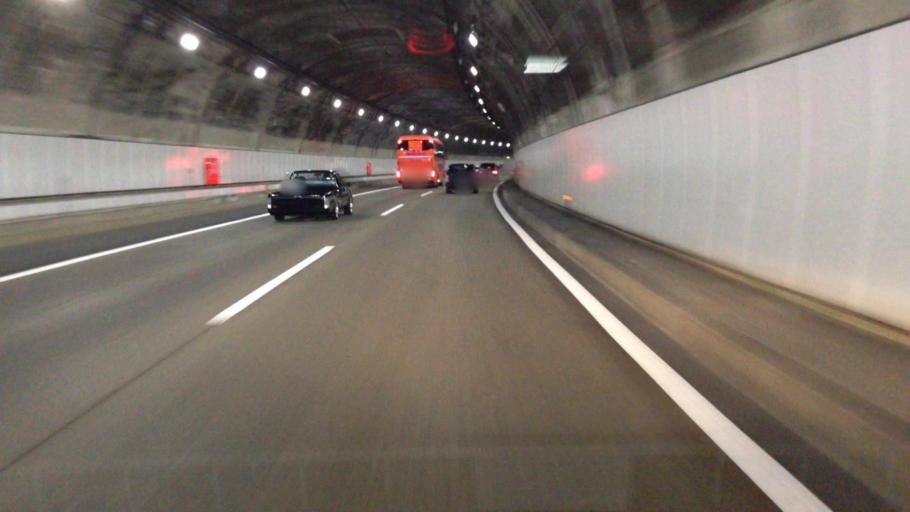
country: JP
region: Kanagawa
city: Zushi
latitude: 35.3047
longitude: 139.6100
